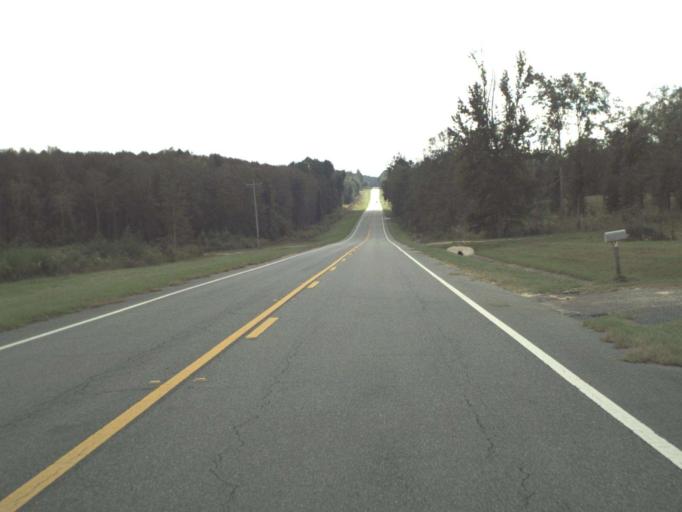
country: US
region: Alabama
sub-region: Geneva County
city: Geneva
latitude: 30.8827
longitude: -85.9500
